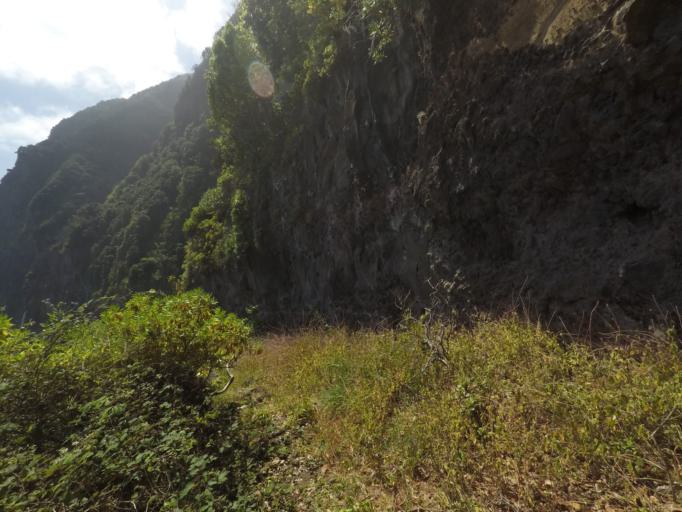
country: PT
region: Madeira
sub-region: Sao Vicente
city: Sao Vicente
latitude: 32.8154
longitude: -17.0945
